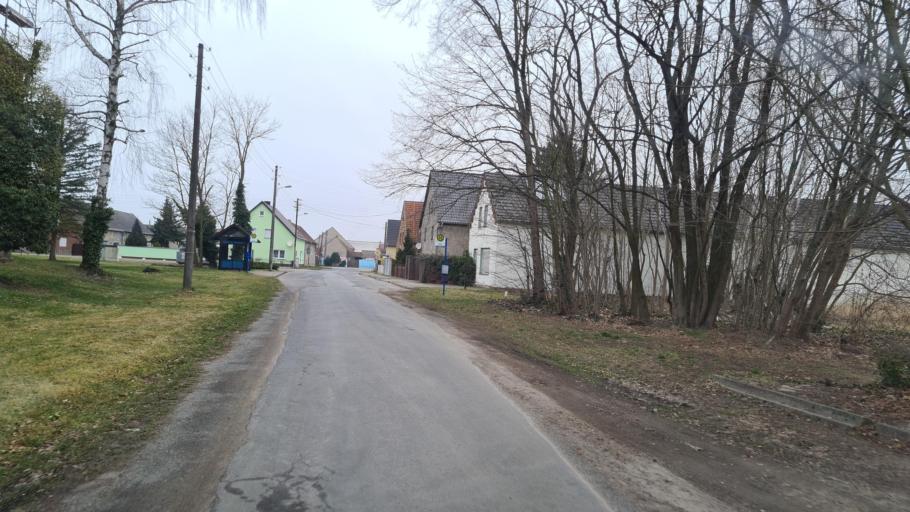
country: DE
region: Brandenburg
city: Herzberg
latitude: 51.6632
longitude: 13.1740
